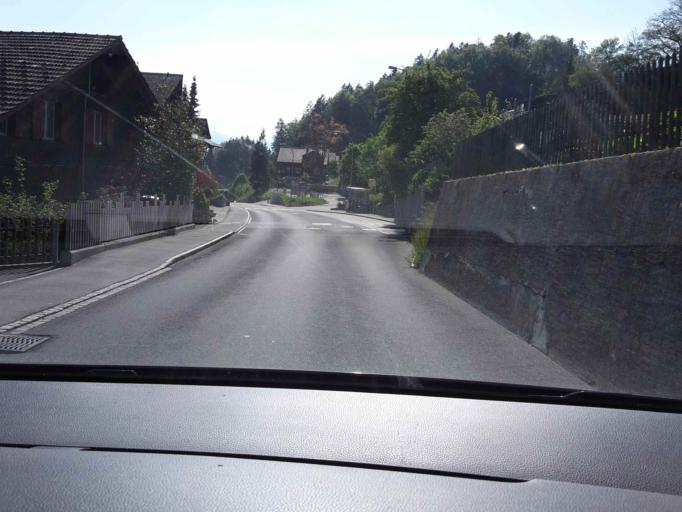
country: CH
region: Bern
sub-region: Thun District
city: Hilterfingen
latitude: 46.7634
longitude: 7.6649
